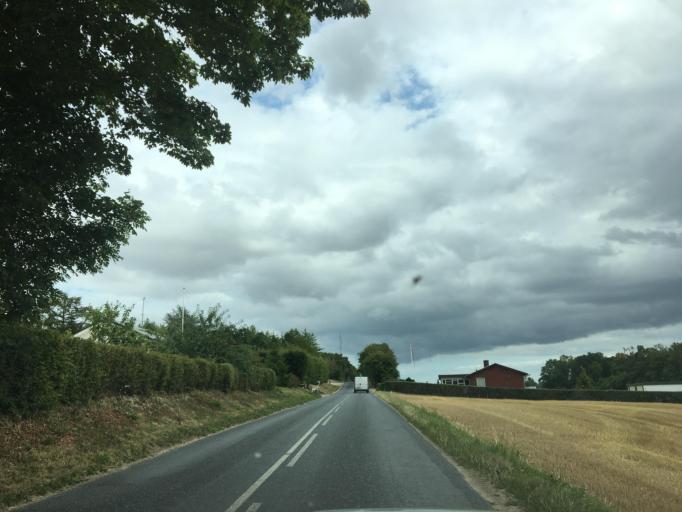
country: DK
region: South Denmark
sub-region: Kerteminde Kommune
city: Langeskov
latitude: 55.3201
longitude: 10.6068
